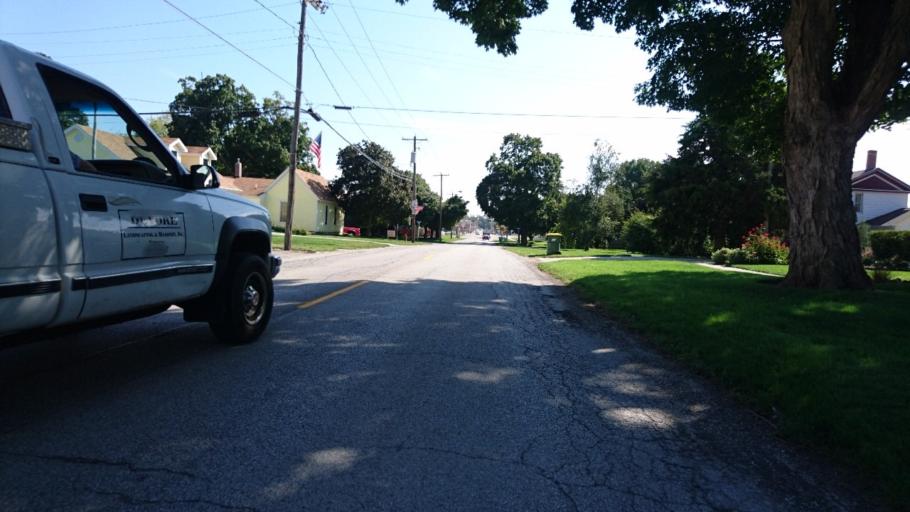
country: US
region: Illinois
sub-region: McLean County
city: Lexington
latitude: 40.6415
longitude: -88.7901
